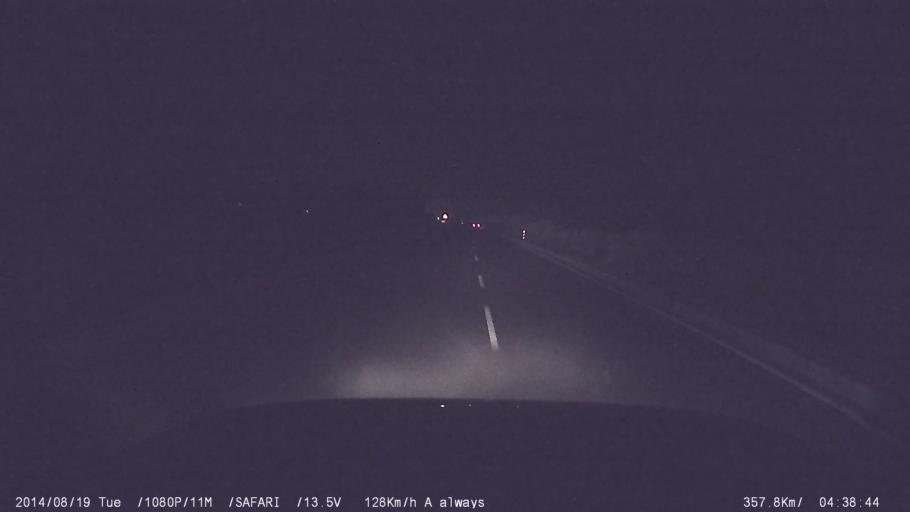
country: IN
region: Tamil Nadu
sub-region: Erode
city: Erode
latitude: 11.3570
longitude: 77.6452
